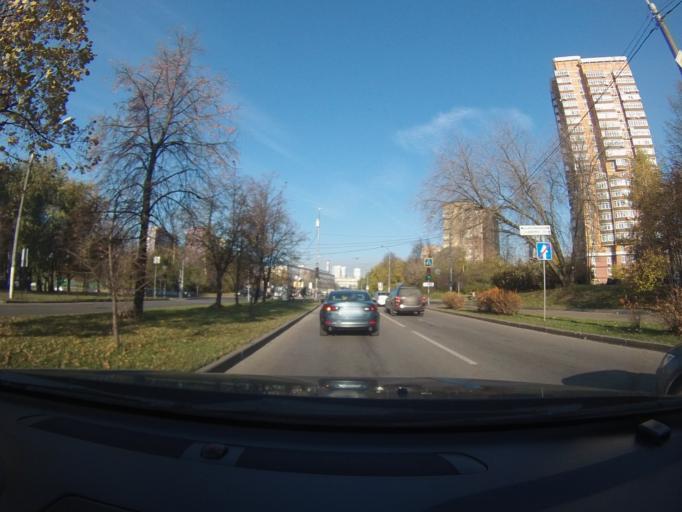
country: RU
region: Moscow
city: Golovinskiy
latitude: 55.8587
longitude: 37.4897
